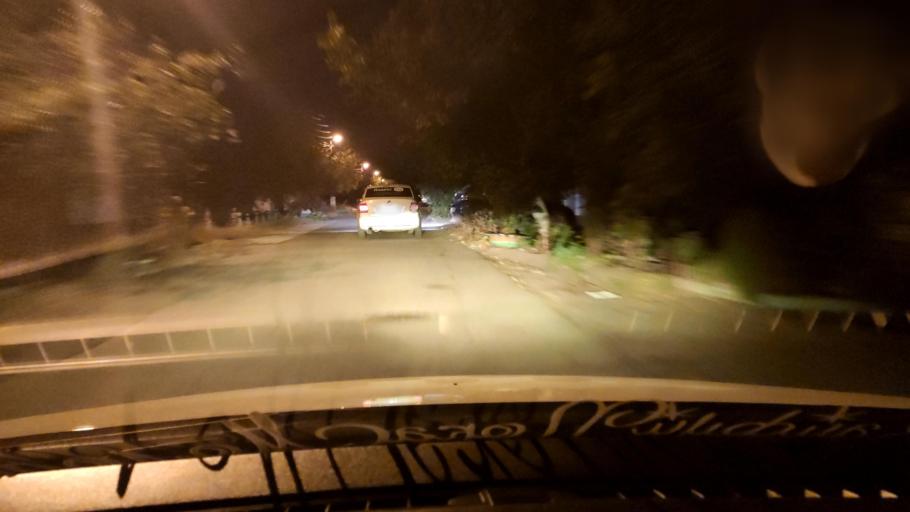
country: RU
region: Voronezj
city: Voronezh
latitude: 51.6416
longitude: 39.1687
